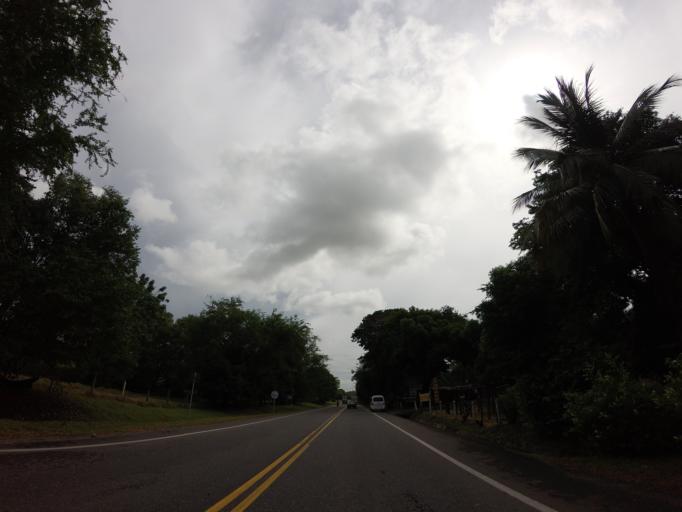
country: CO
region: Caldas
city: La Dorada
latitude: 5.3713
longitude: -74.7178
